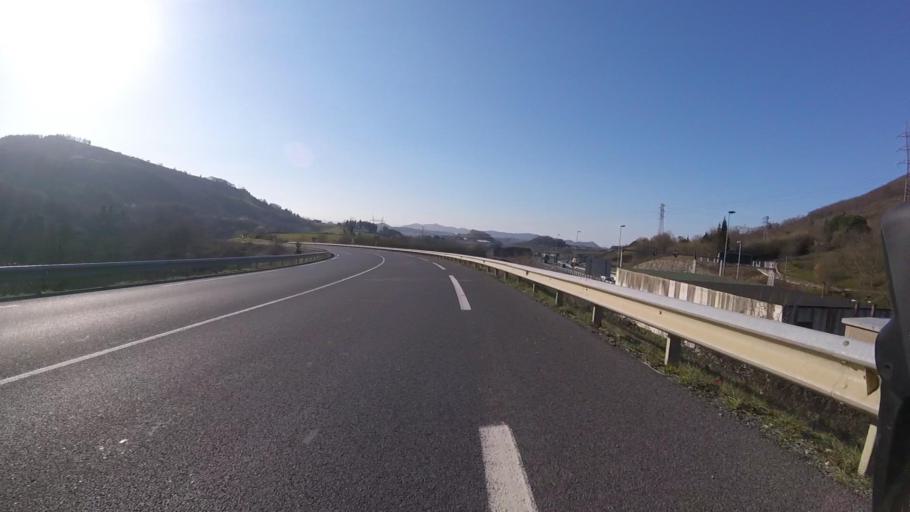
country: ES
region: Basque Country
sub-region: Provincia de Guipuzcoa
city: Astigarraga
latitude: 43.2830
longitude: -1.9202
